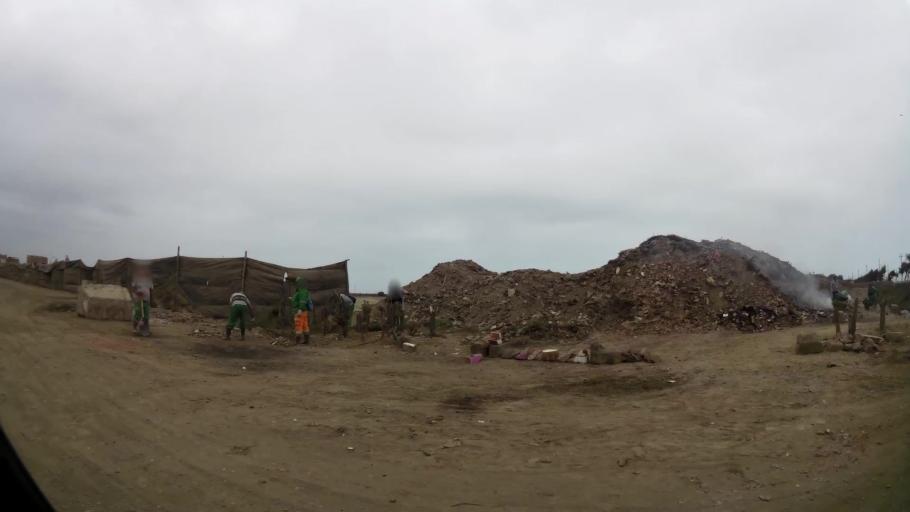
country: PE
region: Lima
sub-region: Barranca
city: Paramonga
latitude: -10.6796
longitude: -77.8228
